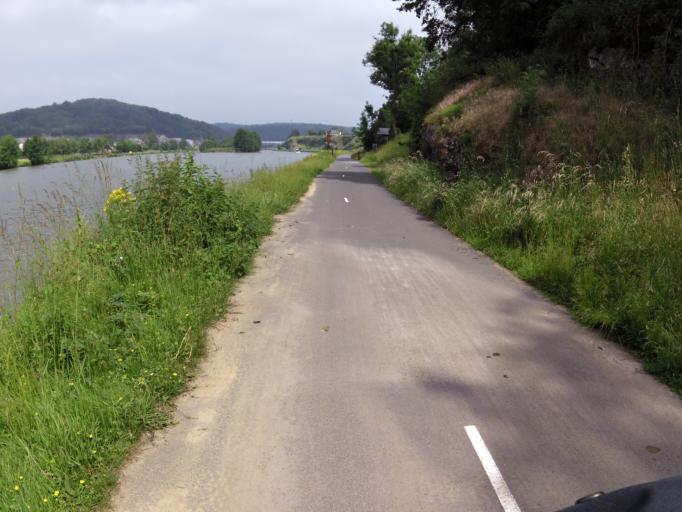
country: FR
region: Champagne-Ardenne
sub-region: Departement des Ardennes
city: Vireux-Molhain
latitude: 50.0769
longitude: 4.7286
